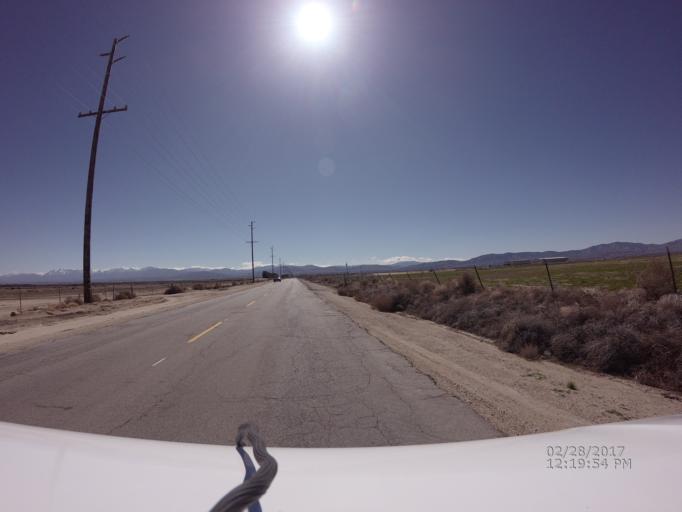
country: US
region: California
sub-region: Los Angeles County
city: Palmdale
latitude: 34.6256
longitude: -118.0588
